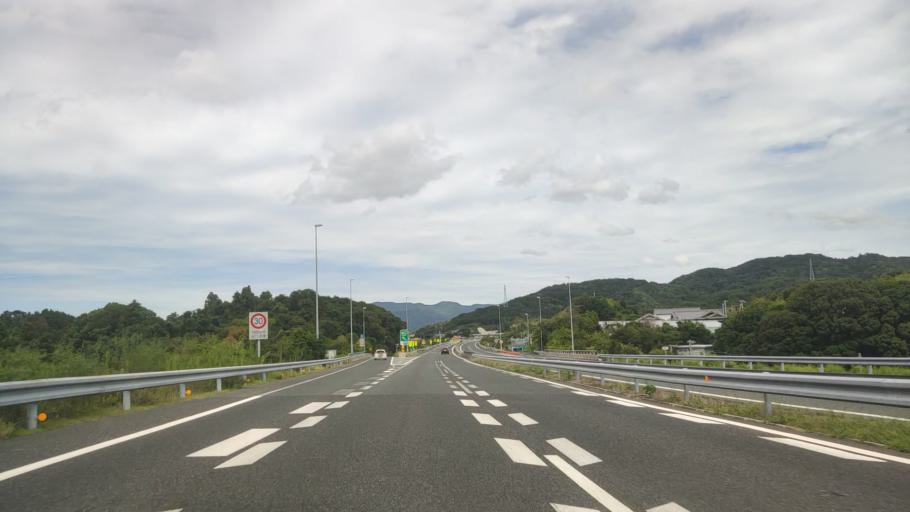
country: JP
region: Wakayama
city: Gobo
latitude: 33.8850
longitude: 135.1826
